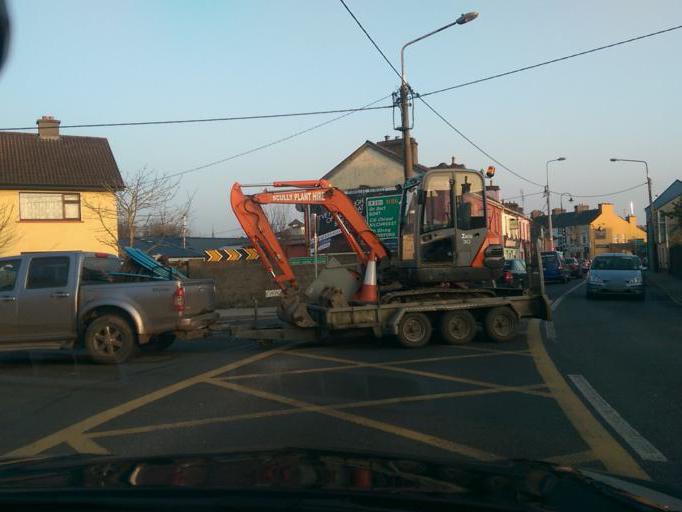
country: IE
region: Connaught
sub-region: County Galway
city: Loughrea
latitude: 53.2000
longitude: -8.5745
